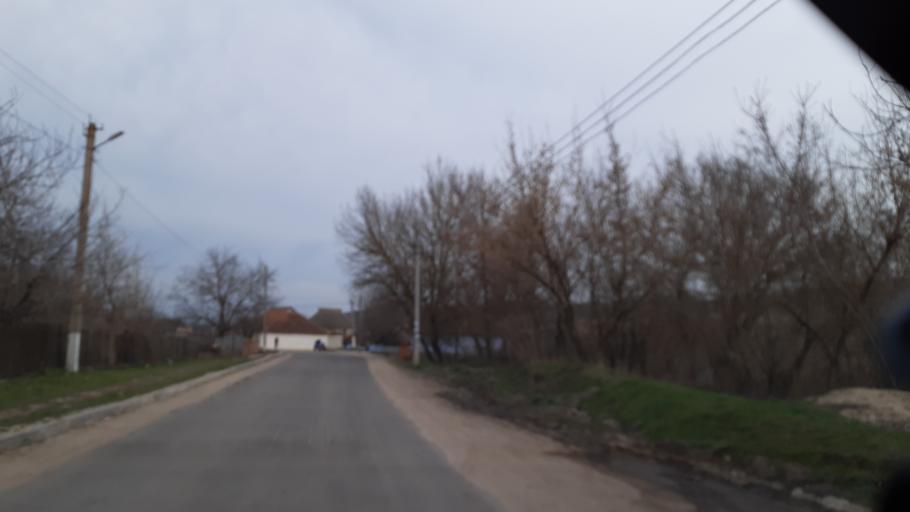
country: MD
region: Soldanesti
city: Soldanesti
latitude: 47.6843
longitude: 28.7587
